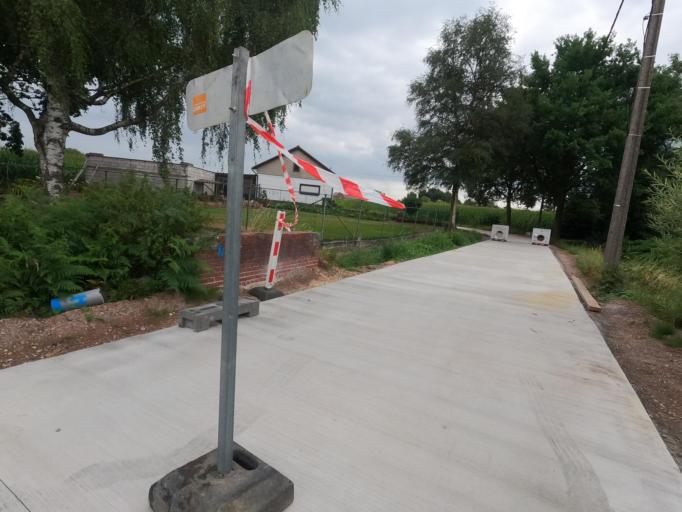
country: BE
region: Flanders
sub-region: Provincie Antwerpen
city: Rijkevorsel
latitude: 51.3553
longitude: 4.7484
